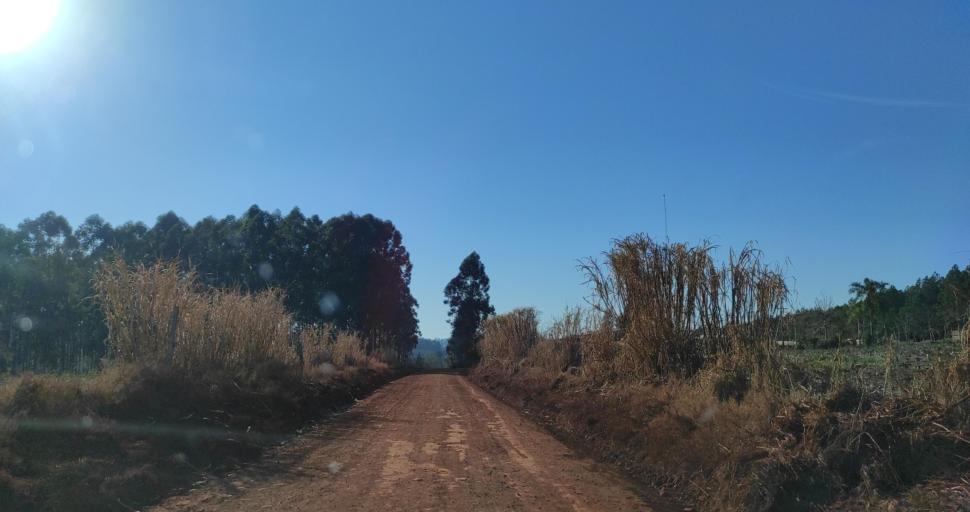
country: AR
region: Misiones
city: Capiovi
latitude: -26.8801
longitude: -55.0384
